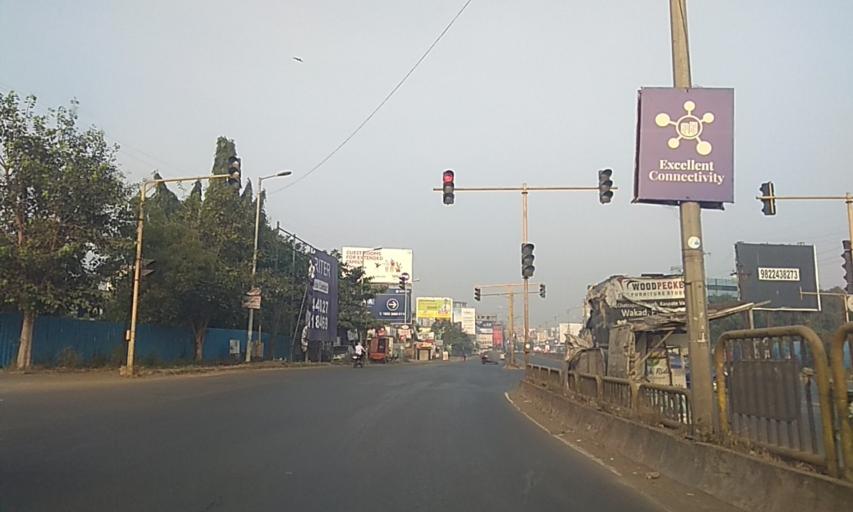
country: IN
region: Maharashtra
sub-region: Pune Division
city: Pimpri
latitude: 18.5901
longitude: 73.7688
